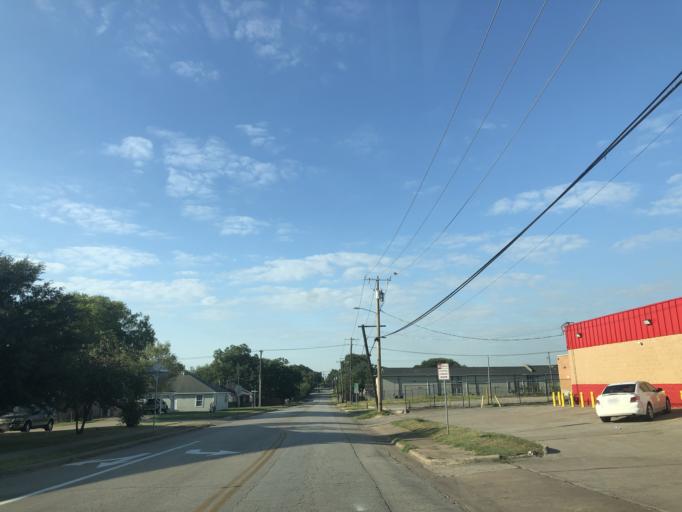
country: US
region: Texas
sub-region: Dallas County
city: Grand Prairie
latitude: 32.7390
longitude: -97.0357
